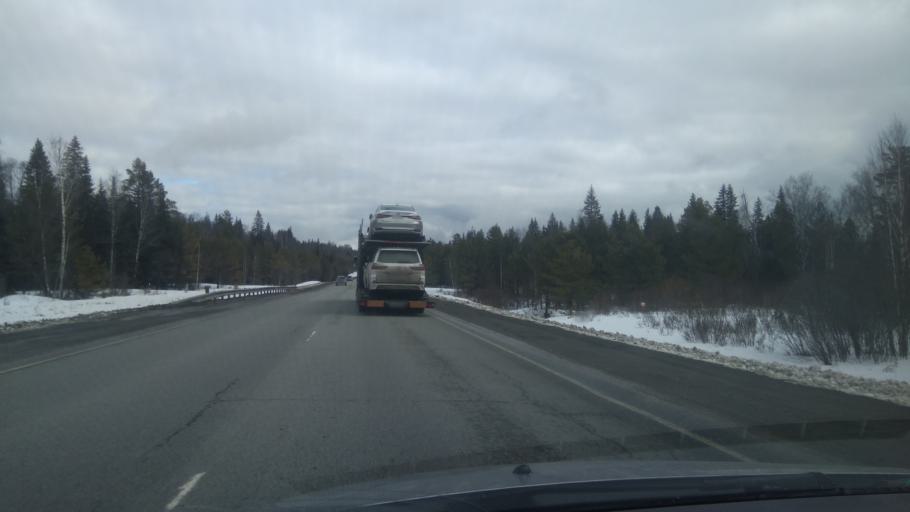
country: RU
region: Sverdlovsk
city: Nizhniye Sergi
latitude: 56.8250
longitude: 59.2622
